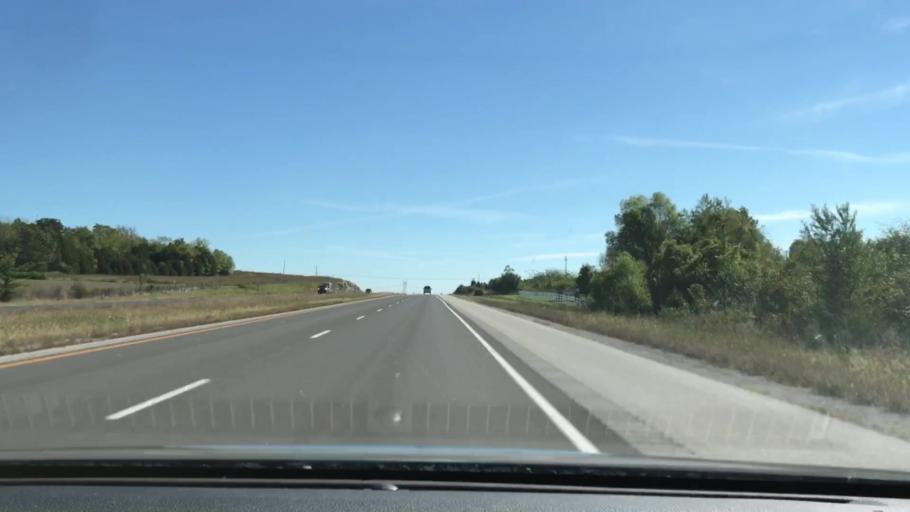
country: US
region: Kentucky
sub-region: Logan County
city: Russellville
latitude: 36.8370
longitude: -86.9400
